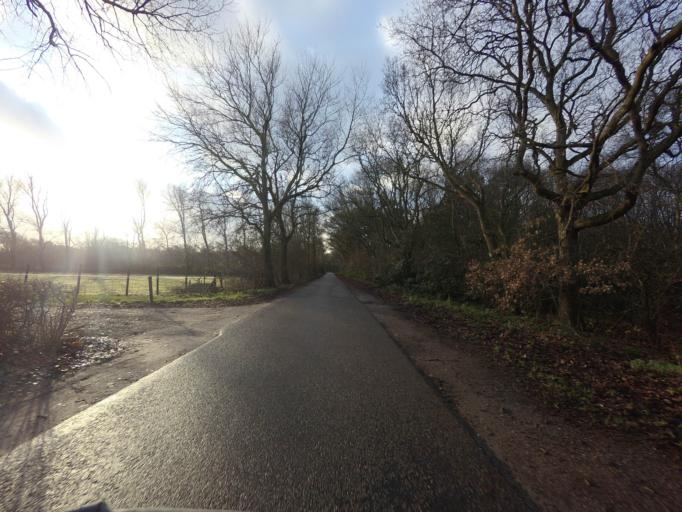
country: NL
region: North Holland
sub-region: Gemeente Texel
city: Den Burg
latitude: 53.0977
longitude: 4.7735
